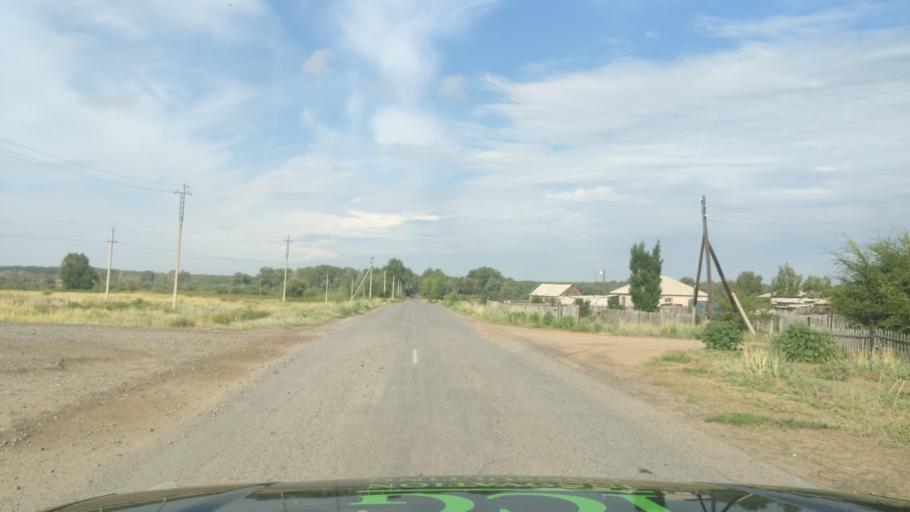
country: KZ
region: Pavlodar
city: Leninskiy
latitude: 52.4774
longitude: 76.8175
